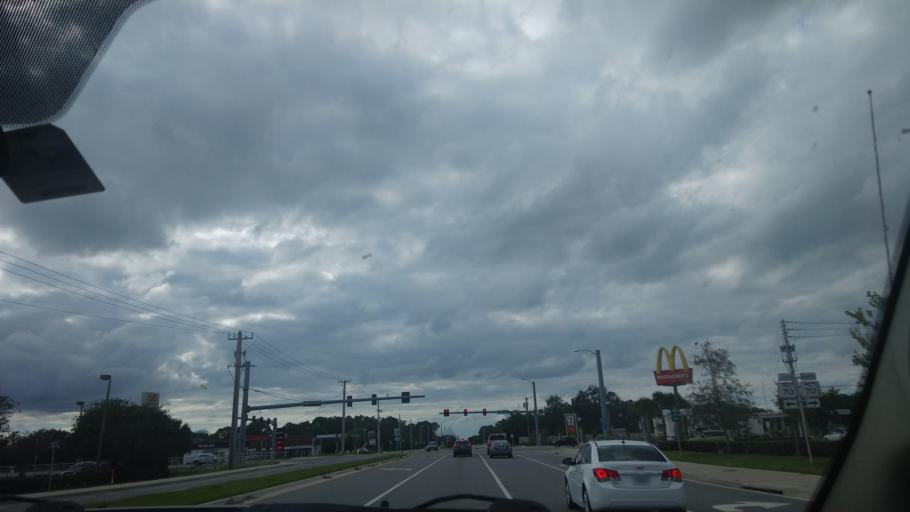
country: US
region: Florida
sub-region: Saint Lucie County
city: Lakewood Park
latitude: 27.5212
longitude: -80.3974
